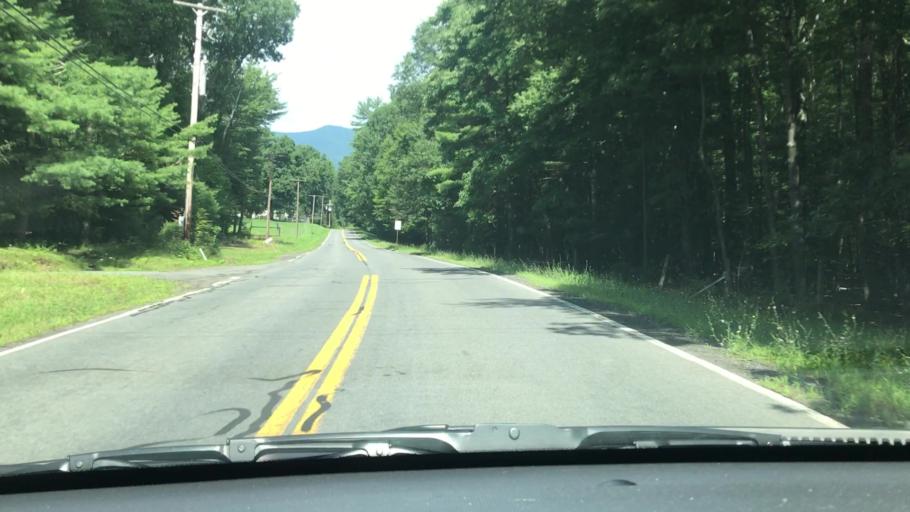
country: US
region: New York
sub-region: Ulster County
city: Shokan
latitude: 41.9557
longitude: -74.2625
